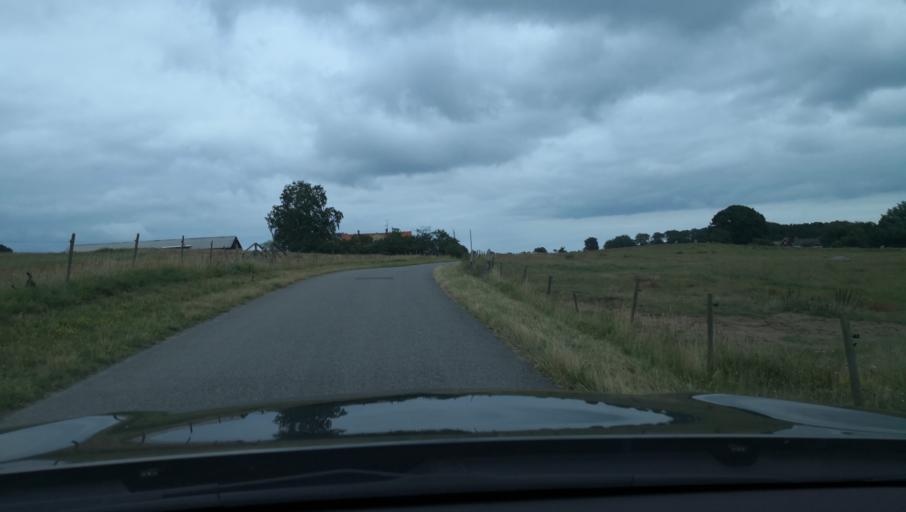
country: SE
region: Skane
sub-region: Simrishamns Kommun
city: Kivik
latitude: 55.7235
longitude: 14.1794
